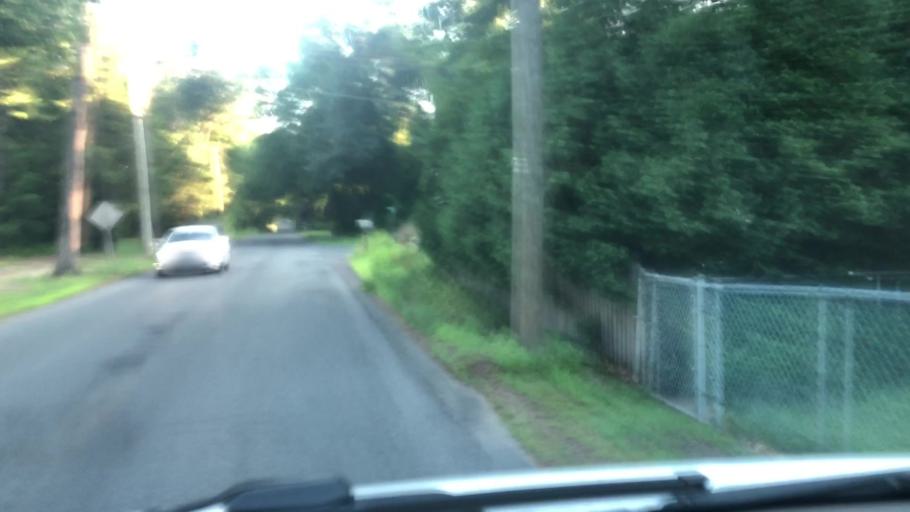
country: US
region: Massachusetts
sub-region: Hampshire County
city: Easthampton
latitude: 42.2837
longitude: -72.7139
